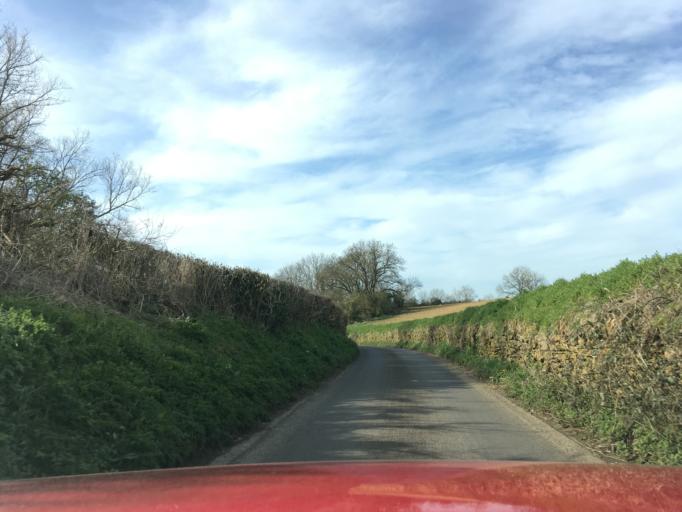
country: GB
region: England
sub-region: Wiltshire
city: Luckington
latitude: 51.5455
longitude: -2.2384
